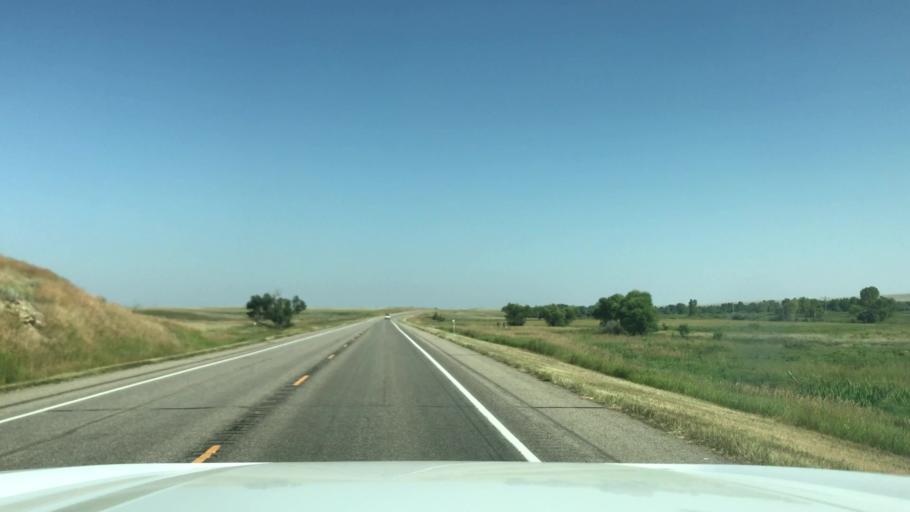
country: US
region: Montana
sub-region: Wheatland County
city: Harlowton
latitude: 46.4140
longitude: -109.7079
